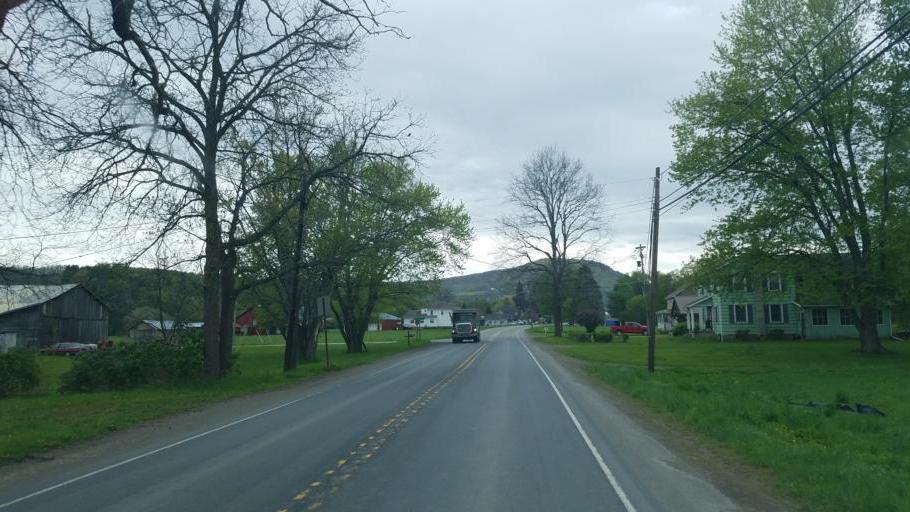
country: US
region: Pennsylvania
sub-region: Tioga County
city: Westfield
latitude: 41.9253
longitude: -77.5242
